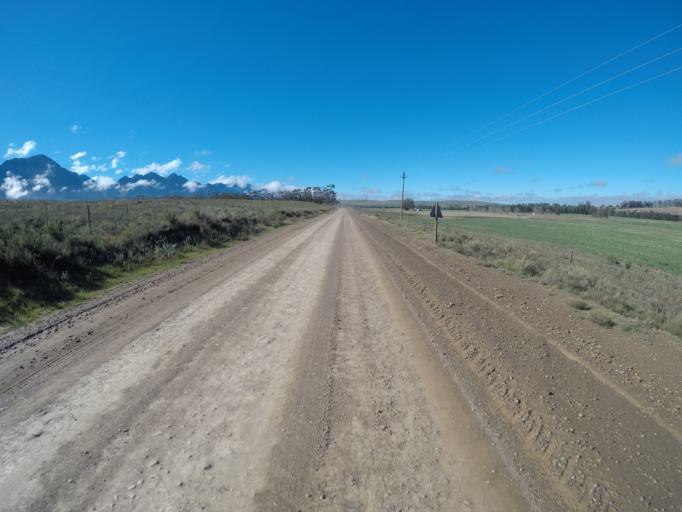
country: ZA
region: Western Cape
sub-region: Overberg District Municipality
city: Caledon
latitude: -34.0968
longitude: 19.6748
